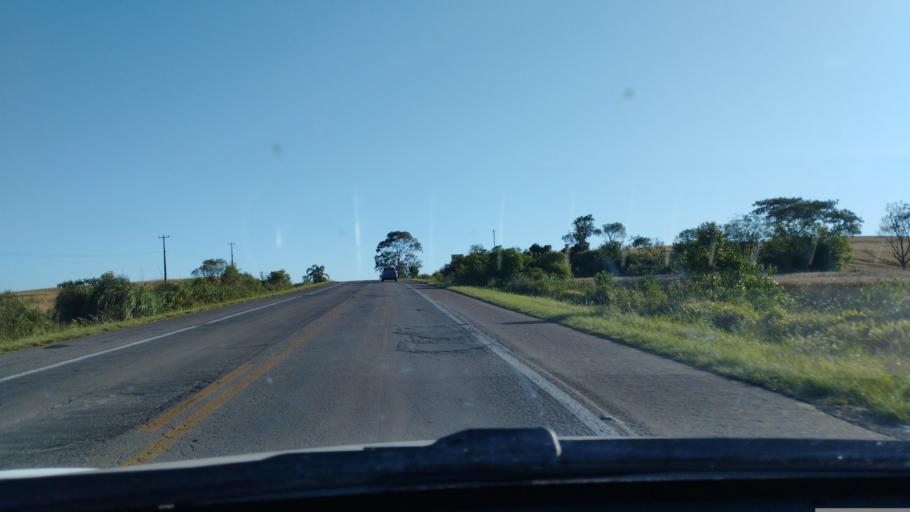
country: BR
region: Rio Grande do Sul
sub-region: Julio De Castilhos
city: Julio de Castilhos
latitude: -29.4136
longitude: -53.6698
